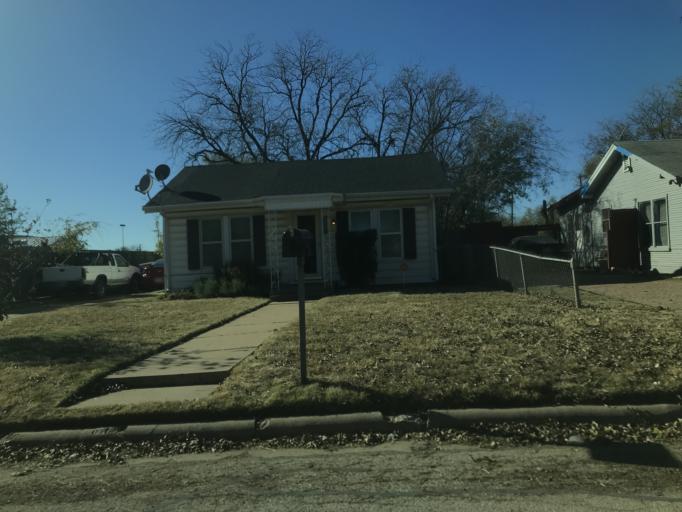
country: US
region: Texas
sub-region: Taylor County
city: Abilene
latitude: 32.4342
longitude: -99.7570
